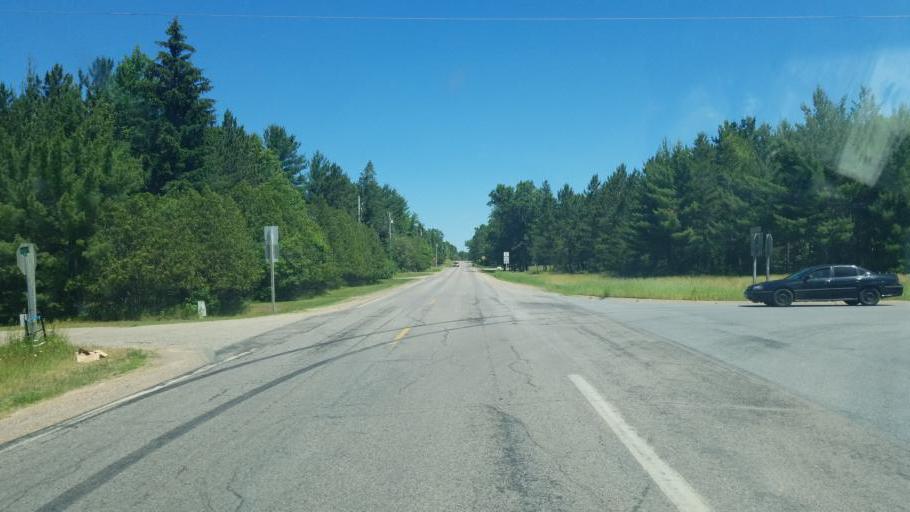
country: US
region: Wisconsin
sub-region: Adams County
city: Adams
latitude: 43.9734
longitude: -89.9379
